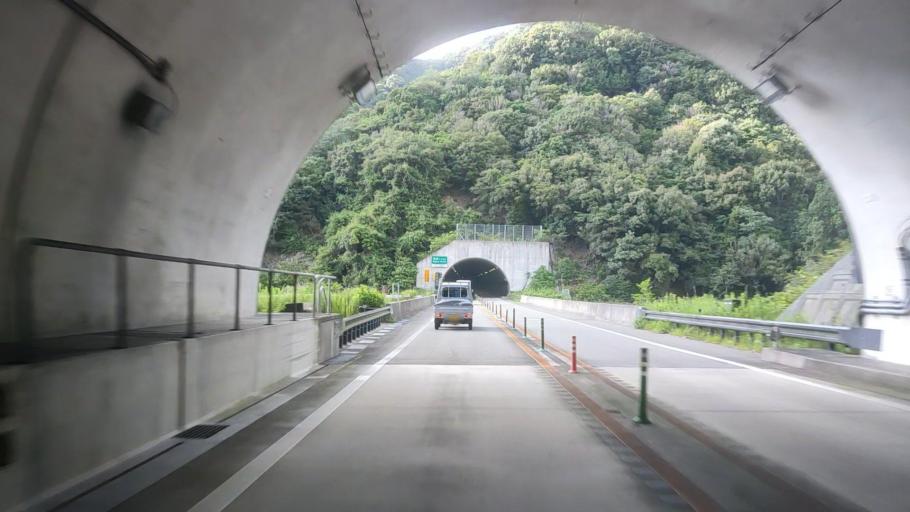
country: JP
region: Wakayama
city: Tanabe
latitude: 33.6124
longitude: 135.4249
